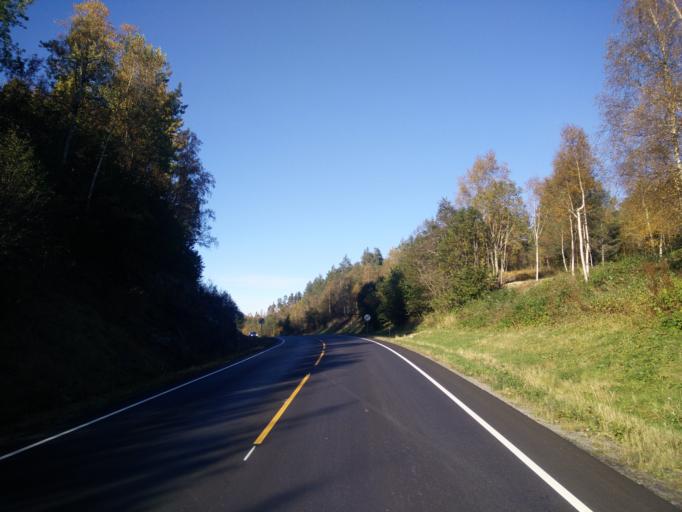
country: NO
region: More og Romsdal
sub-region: Halsa
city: Liaboen
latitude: 63.0905
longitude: 8.3519
